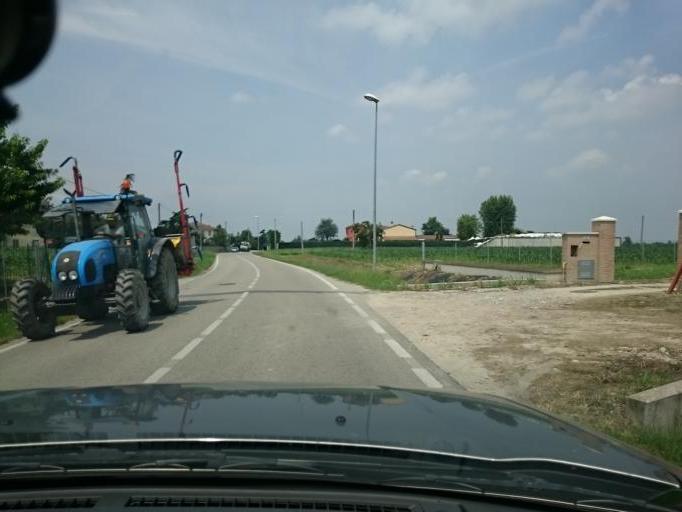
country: IT
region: Veneto
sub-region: Provincia di Padova
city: Brugine
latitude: 45.3153
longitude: 11.9907
